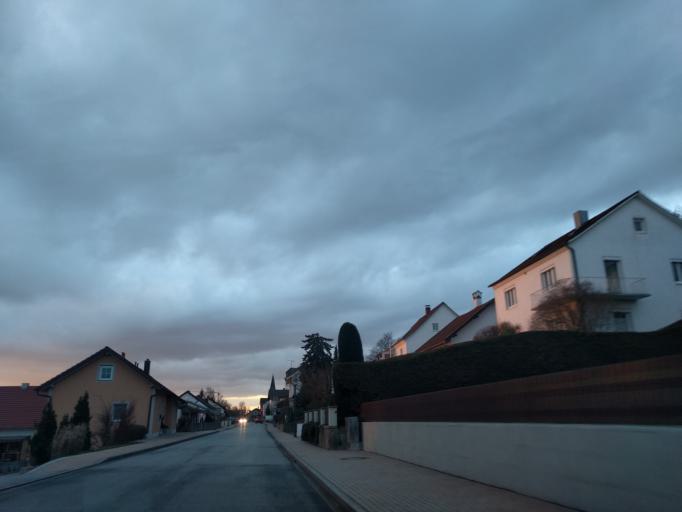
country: DE
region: Bavaria
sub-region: Lower Bavaria
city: Winzer
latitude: 48.7202
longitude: 13.0819
